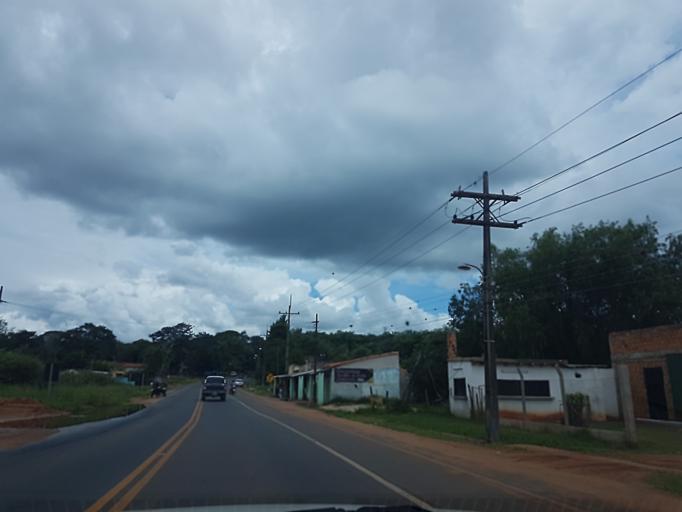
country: PY
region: Central
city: Limpio
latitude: -25.2370
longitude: -57.4394
